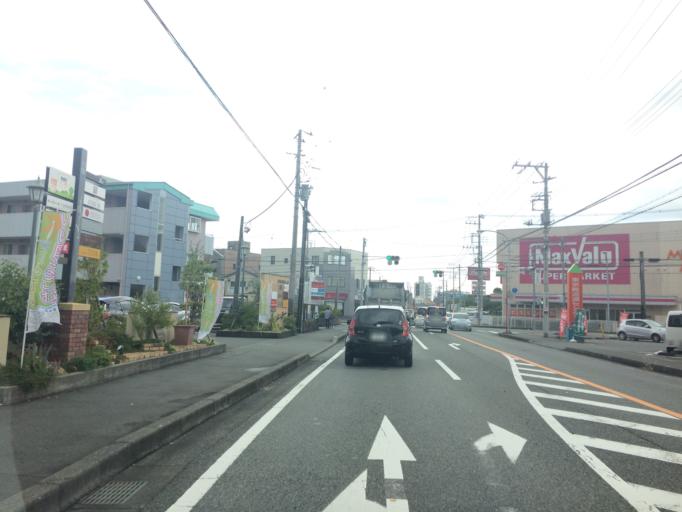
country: JP
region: Shizuoka
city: Fuji
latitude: 35.1622
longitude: 138.6499
